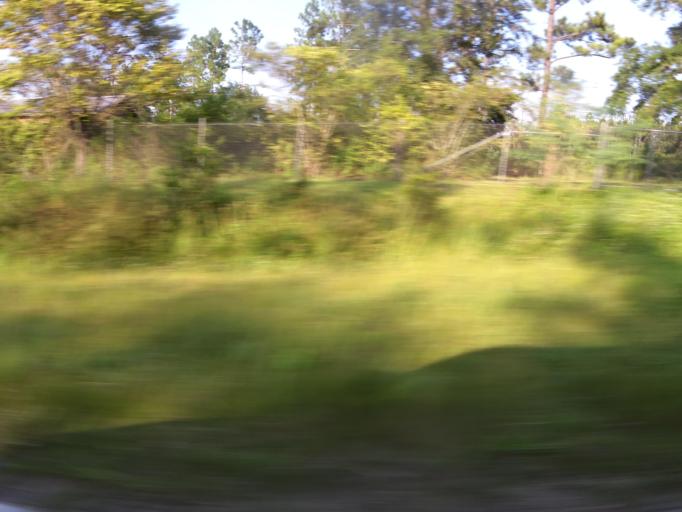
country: US
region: Florida
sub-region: Duval County
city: Baldwin
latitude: 30.3646
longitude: -82.0121
